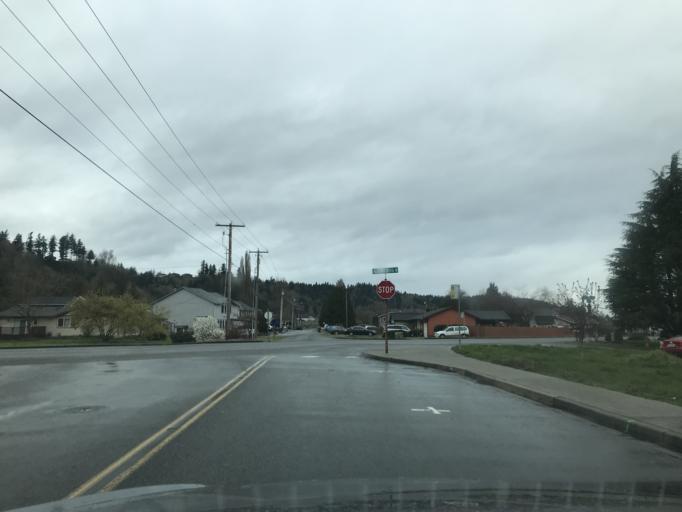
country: US
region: Washington
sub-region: King County
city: Algona
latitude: 47.2860
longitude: -122.2555
